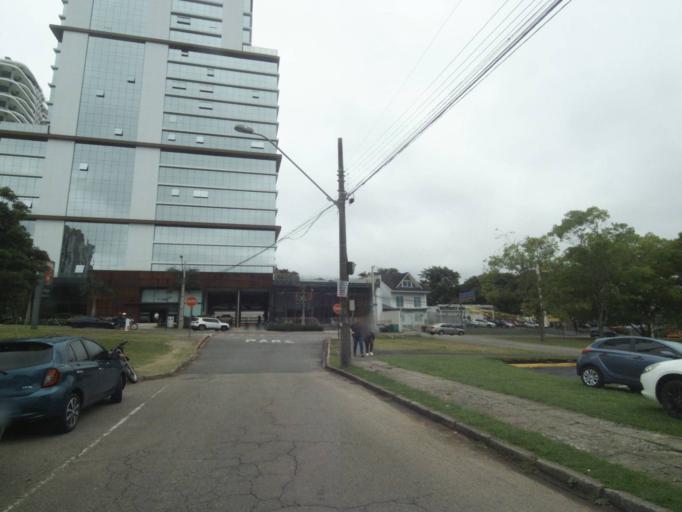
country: BR
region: Parana
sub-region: Curitiba
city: Curitiba
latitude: -25.4359
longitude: -49.3082
